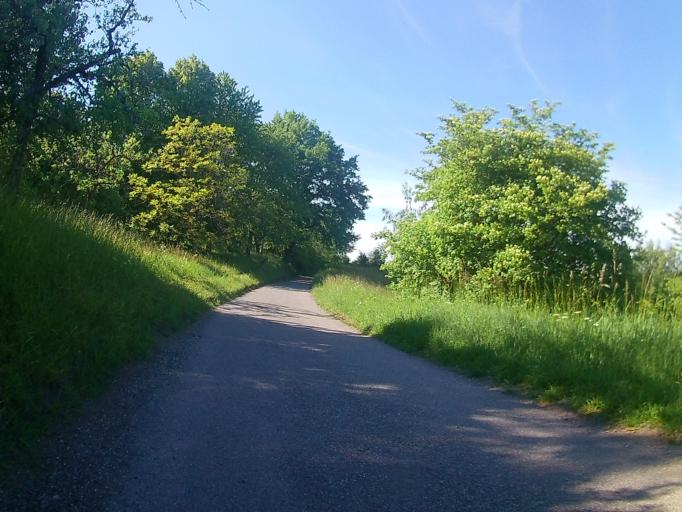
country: DE
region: Baden-Wuerttemberg
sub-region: Regierungsbezirk Stuttgart
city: Fellbach
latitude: 48.7802
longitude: 9.2906
